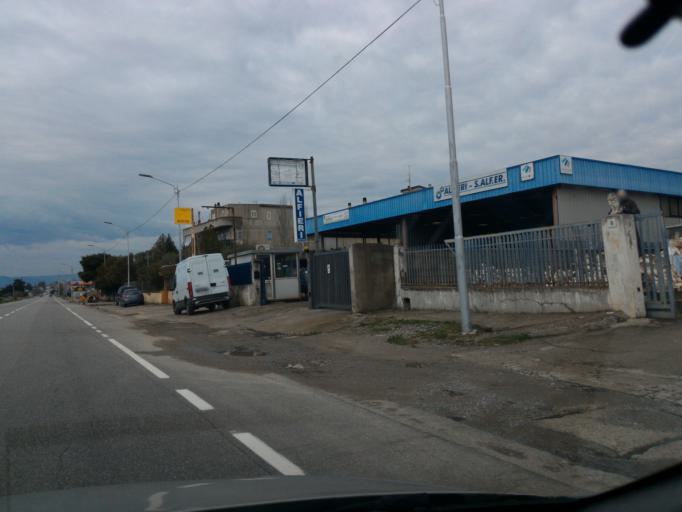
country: IT
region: Calabria
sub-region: Provincia di Catanzaro
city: Barone
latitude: 38.8468
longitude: 16.6579
